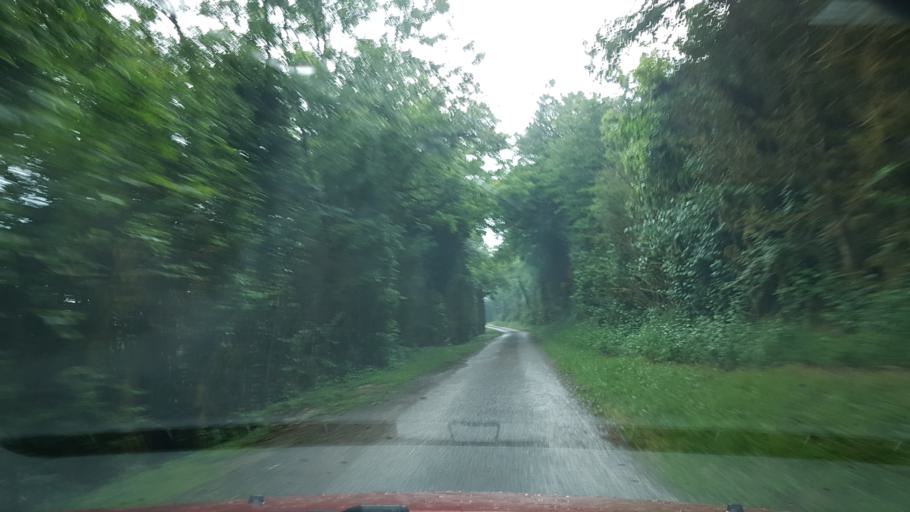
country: FR
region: Franche-Comte
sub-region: Departement du Jura
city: Clairvaux-les-Lacs
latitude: 46.5290
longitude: 5.7148
